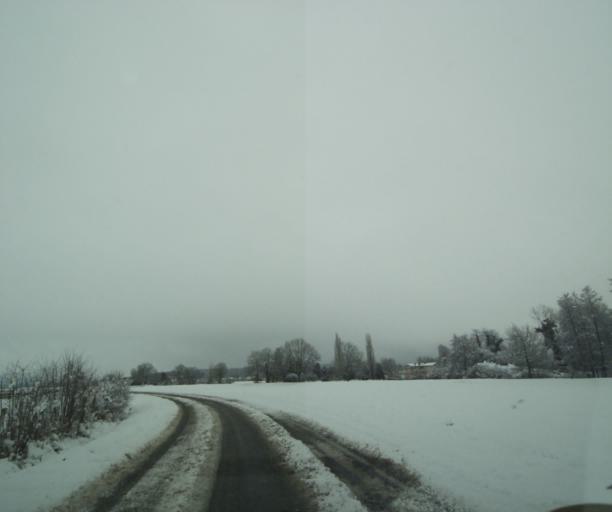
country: FR
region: Champagne-Ardenne
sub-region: Departement de la Haute-Marne
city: Saint-Dizier
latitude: 48.5678
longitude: 4.8913
